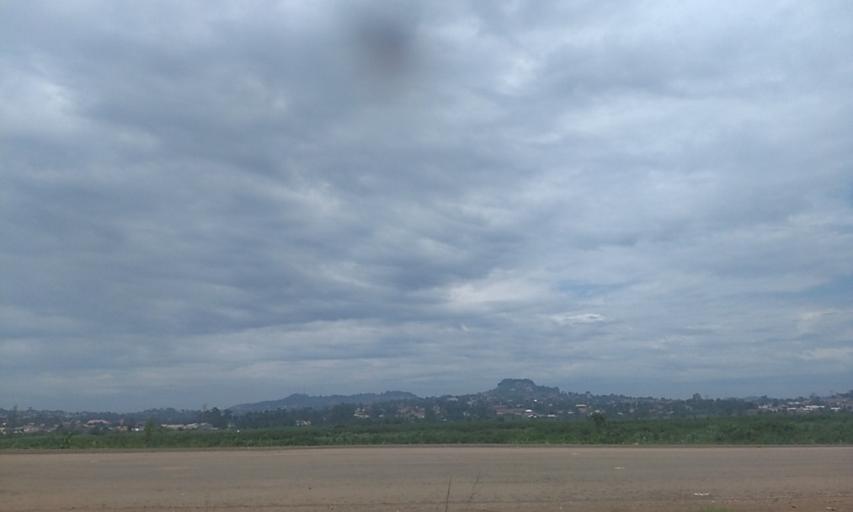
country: UG
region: Central Region
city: Kampala Central Division
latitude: 0.3150
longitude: 32.5180
